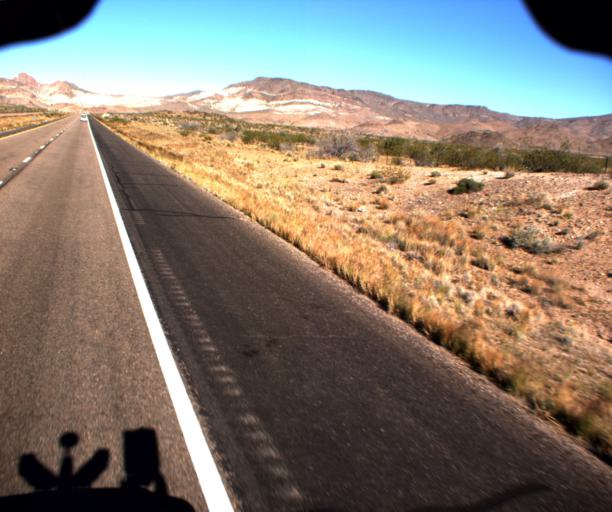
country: US
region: Arizona
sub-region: Mohave County
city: Golden Valley
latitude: 35.2284
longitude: -114.3473
